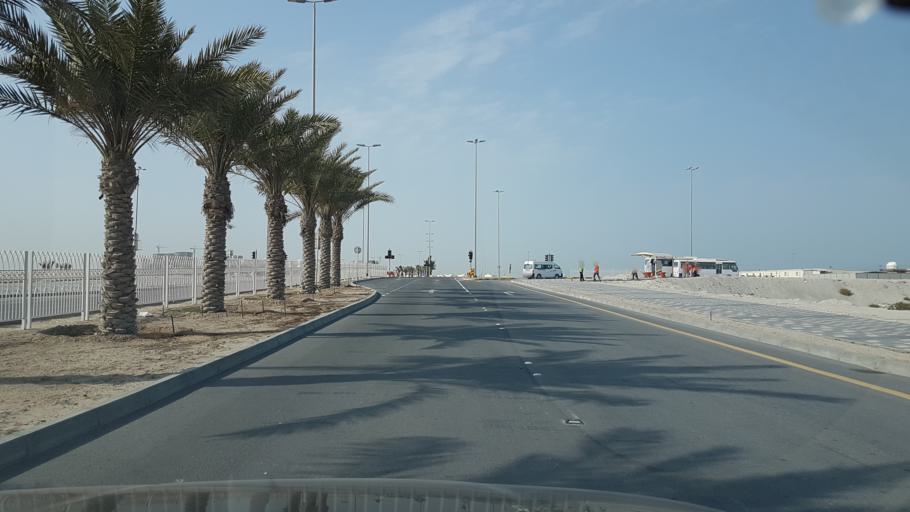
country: BH
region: Muharraq
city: Al Hadd
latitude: 26.2744
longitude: 50.6773
